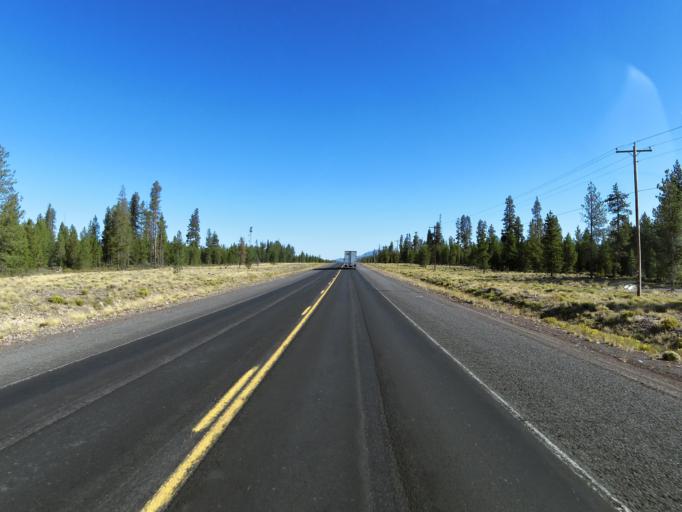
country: US
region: Oregon
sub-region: Deschutes County
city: La Pine
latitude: 43.1422
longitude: -121.7996
